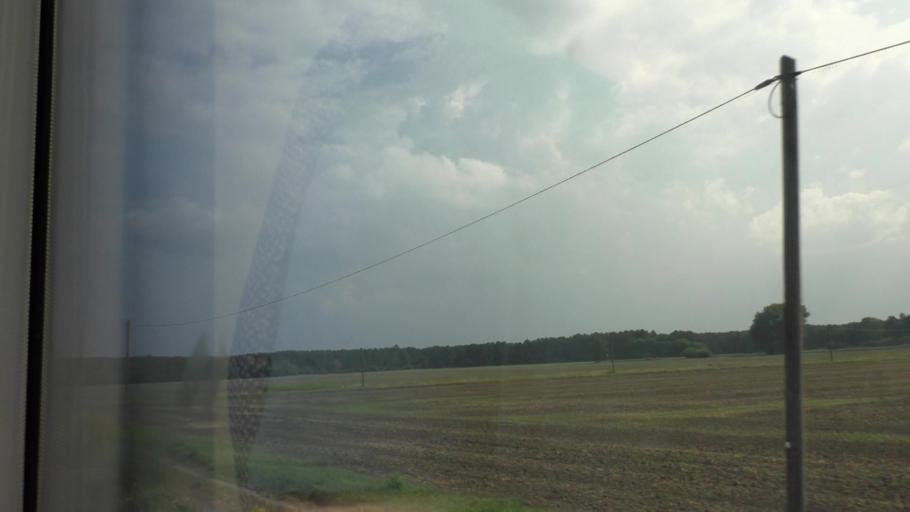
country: DE
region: Brandenburg
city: Spreenhagen
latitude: 52.2915
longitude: 13.7797
